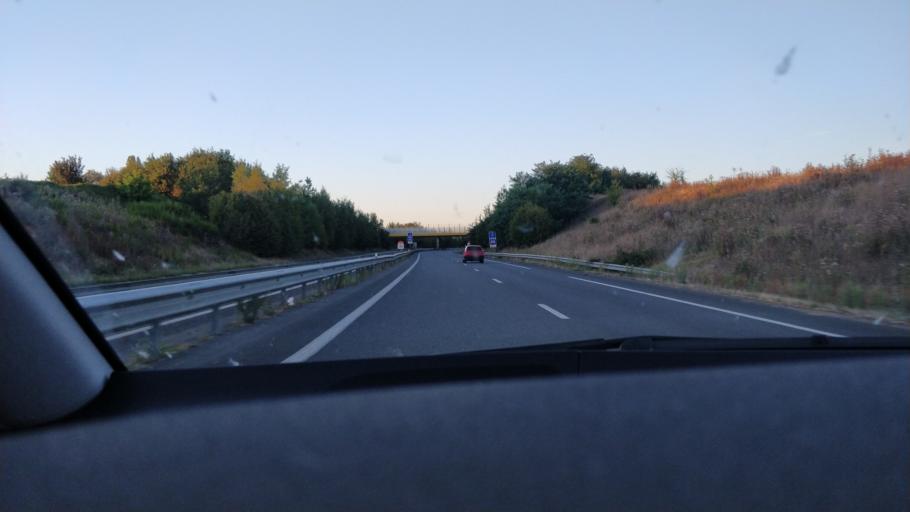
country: FR
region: Poitou-Charentes
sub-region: Departement de la Charente
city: Chasseneuil-sur-Bonnieure
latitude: 45.8199
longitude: 0.4564
